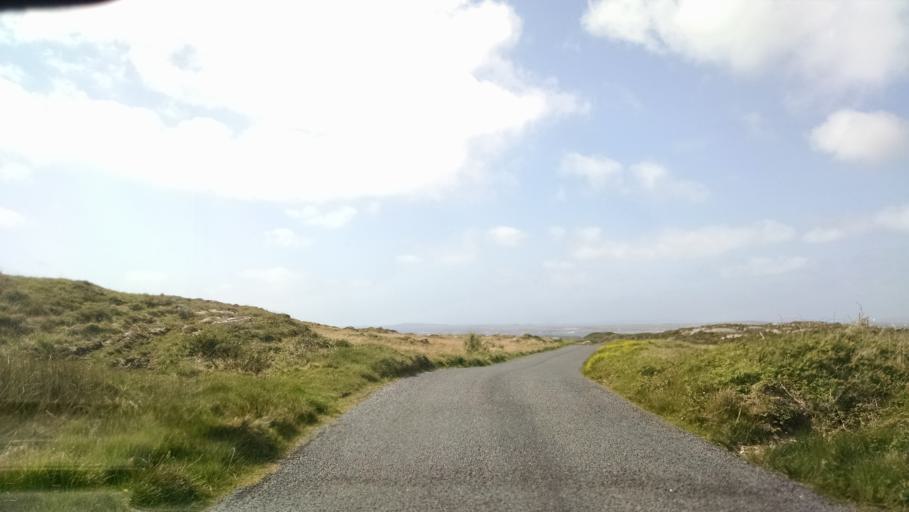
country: IE
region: Connaught
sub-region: County Galway
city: Clifden
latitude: 53.5046
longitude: -10.1048
